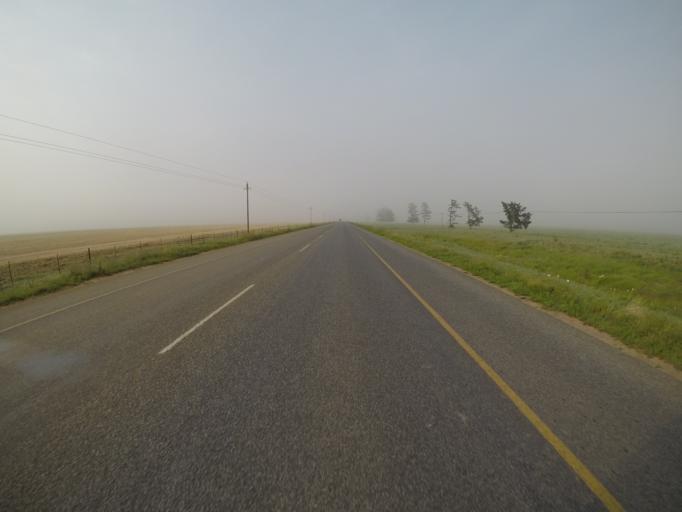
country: ZA
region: Western Cape
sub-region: City of Cape Town
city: Kraaifontein
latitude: -33.6678
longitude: 18.7074
